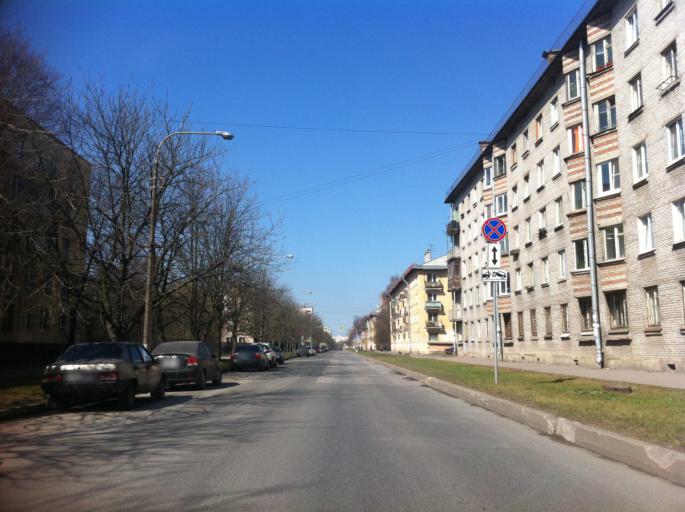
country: RU
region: St.-Petersburg
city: Dachnoye
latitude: 59.8342
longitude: 30.2577
